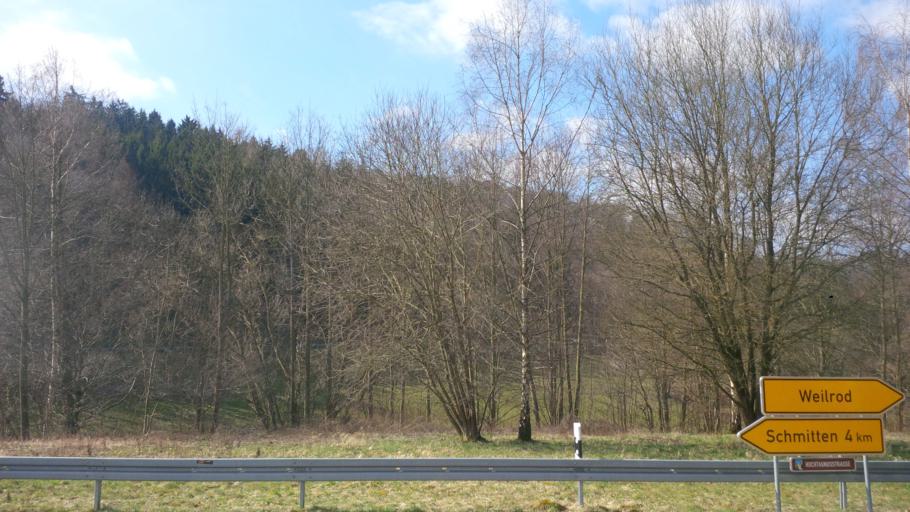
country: DE
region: Hesse
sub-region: Regierungsbezirk Darmstadt
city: Schmitten
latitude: 50.3003
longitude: 8.4584
